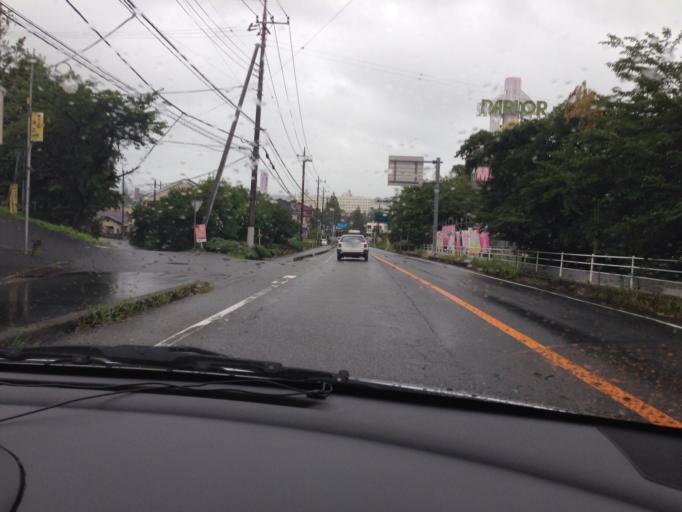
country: JP
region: Ibaraki
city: Ami
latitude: 36.0439
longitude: 140.2195
